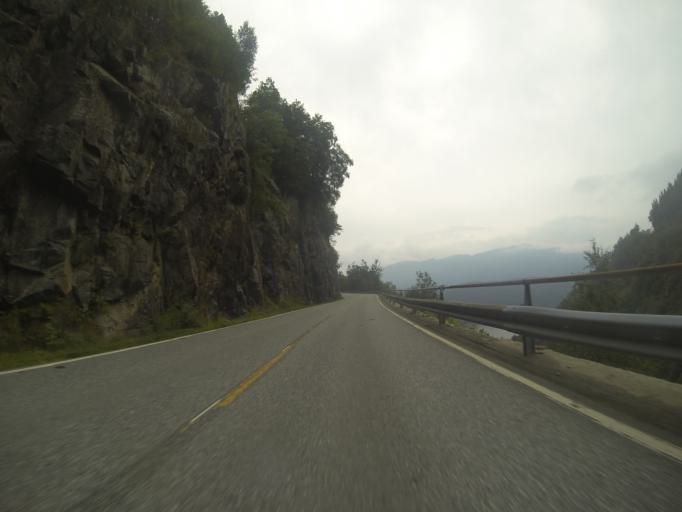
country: NO
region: Rogaland
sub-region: Suldal
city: Sand
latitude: 59.5387
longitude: 6.2562
